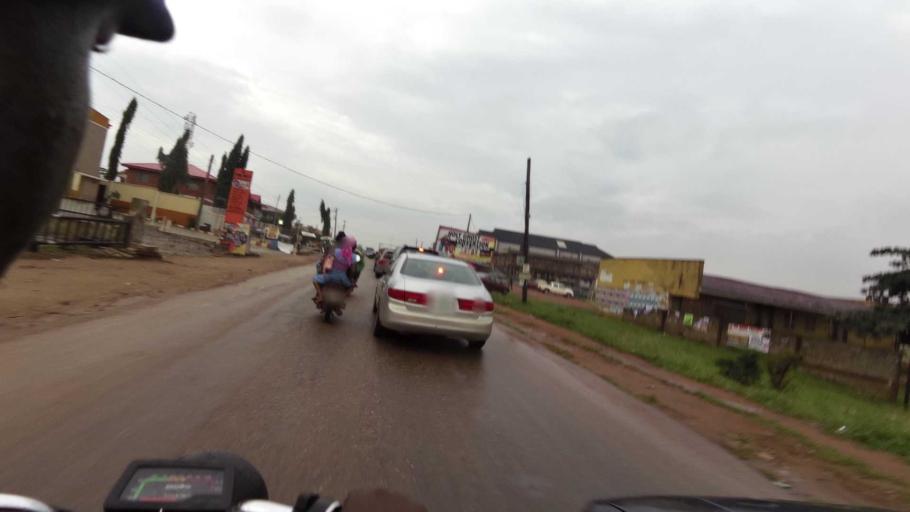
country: NG
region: Oyo
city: Ibadan
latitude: 7.4299
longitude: 3.9401
